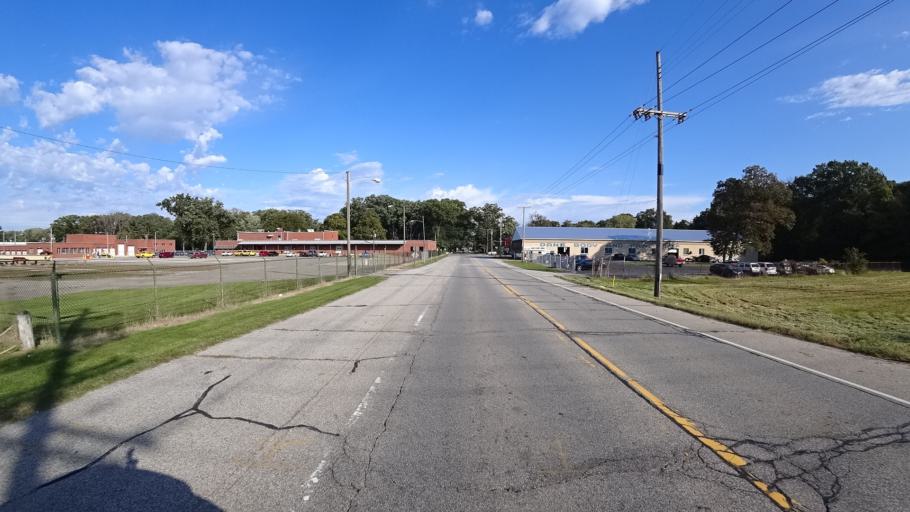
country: US
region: Indiana
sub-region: LaPorte County
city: Trail Creek
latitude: 41.7008
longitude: -86.8746
